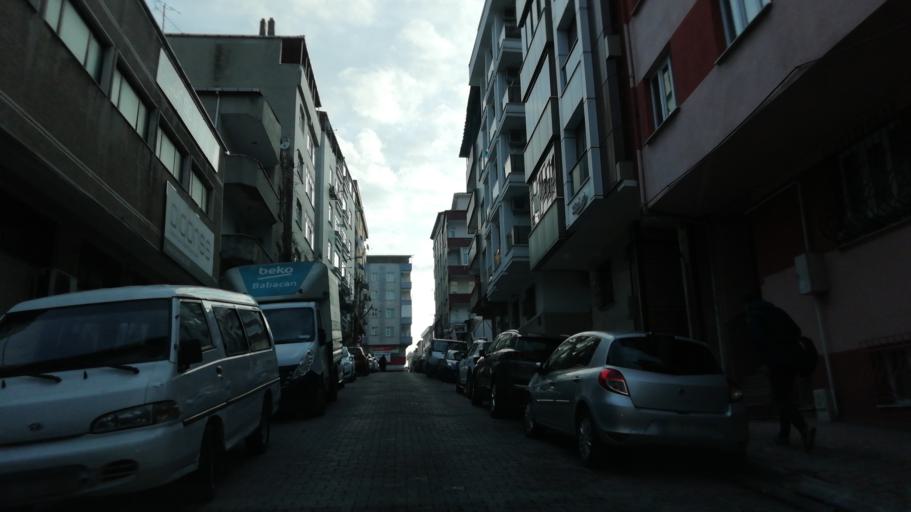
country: TR
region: Istanbul
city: Bahcelievler
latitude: 41.0016
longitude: 28.8290
